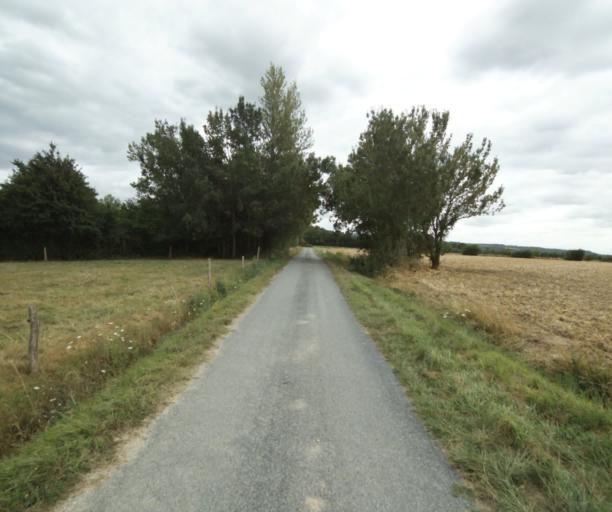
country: FR
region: Midi-Pyrenees
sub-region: Departement du Tarn
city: Soreze
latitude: 43.4736
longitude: 2.0420
